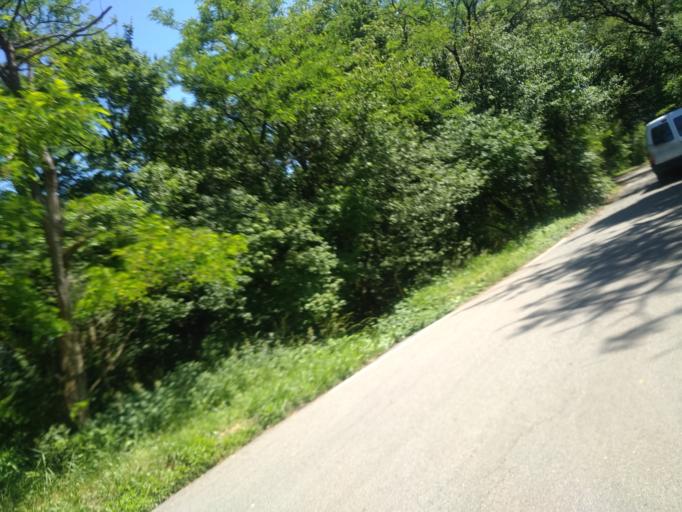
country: FR
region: Rhone-Alpes
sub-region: Departement du Rhone
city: Albigny-sur-Saone
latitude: 45.8548
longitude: 4.8177
